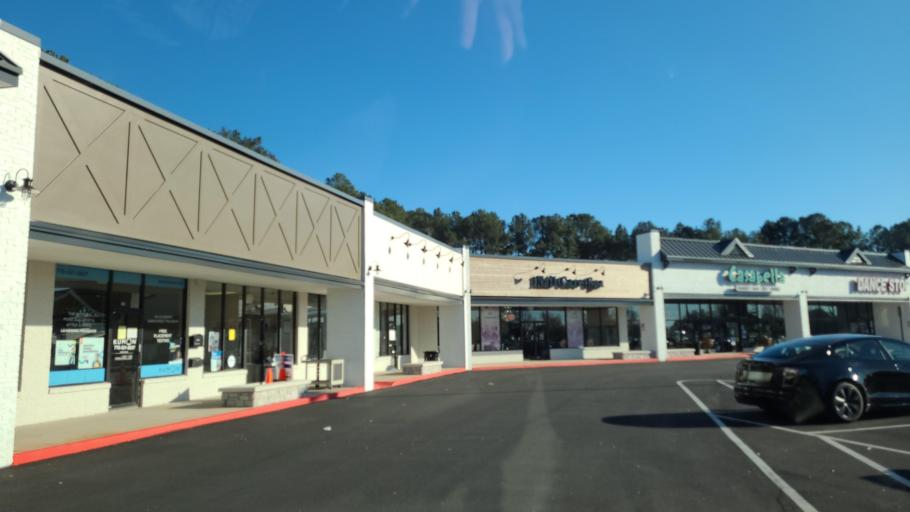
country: US
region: Georgia
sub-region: Fulton County
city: Roswell
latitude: 33.9854
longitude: -84.4221
